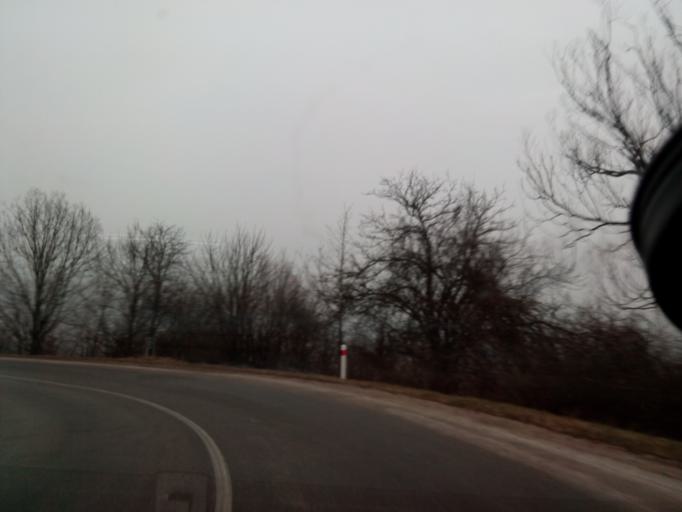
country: SK
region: Kosicky
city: Kosice
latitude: 48.6736
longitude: 21.1555
